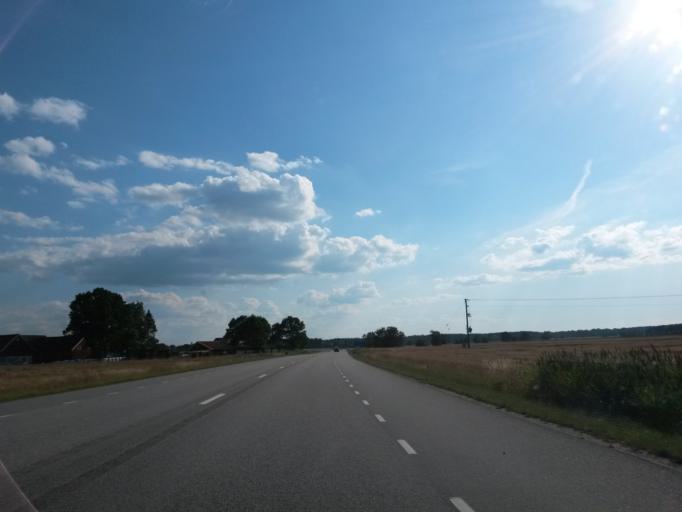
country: SE
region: Vaestra Goetaland
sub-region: Vara Kommun
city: Vara
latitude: 58.2391
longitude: 12.9376
